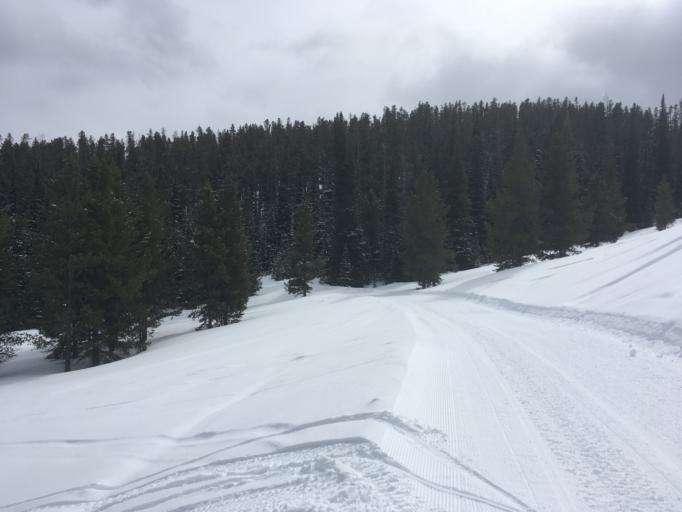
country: US
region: Montana
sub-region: Meagher County
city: White Sulphur Springs
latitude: 46.8444
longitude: -110.7069
